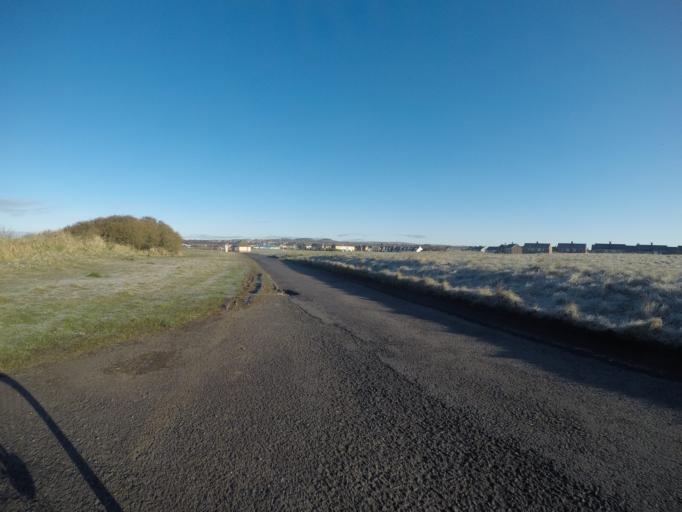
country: GB
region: Scotland
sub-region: North Ayrshire
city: Stevenston
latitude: 55.6289
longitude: -4.7494
